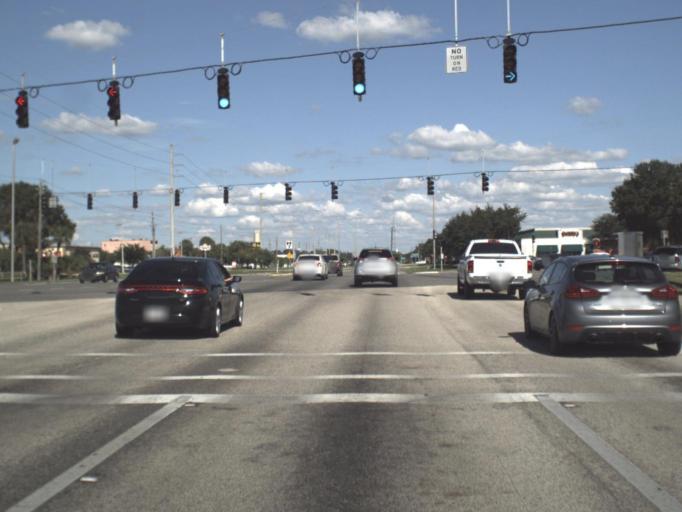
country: US
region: Florida
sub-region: Charlotte County
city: Port Charlotte
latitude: 27.0126
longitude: -82.1466
